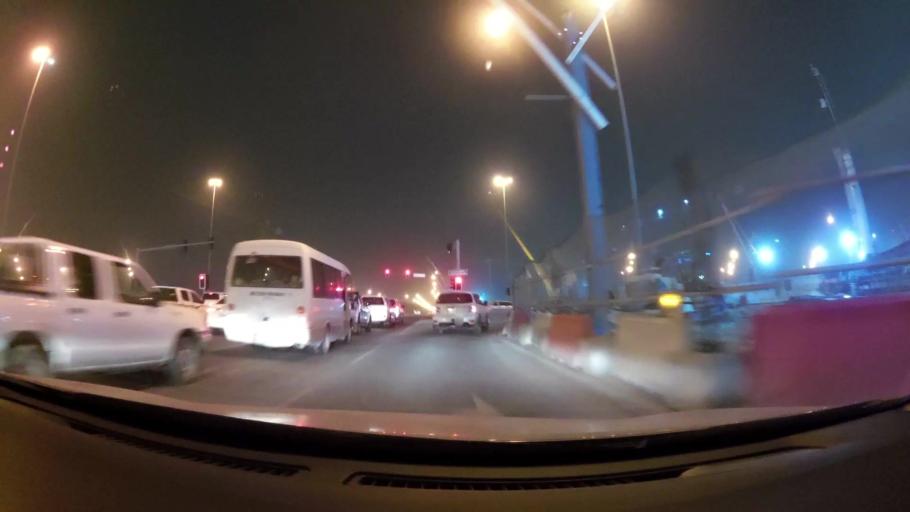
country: QA
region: Baladiyat ar Rayyan
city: Ar Rayyan
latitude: 25.2613
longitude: 51.4539
